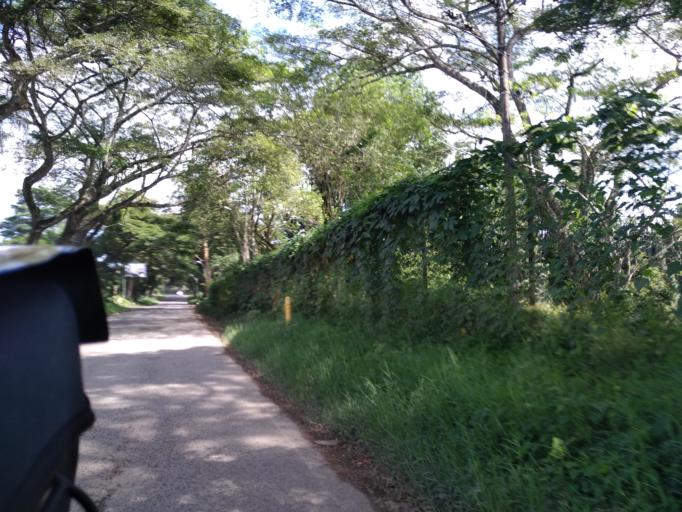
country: CO
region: Valle del Cauca
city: Caicedonia
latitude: 4.3406
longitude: -75.8311
